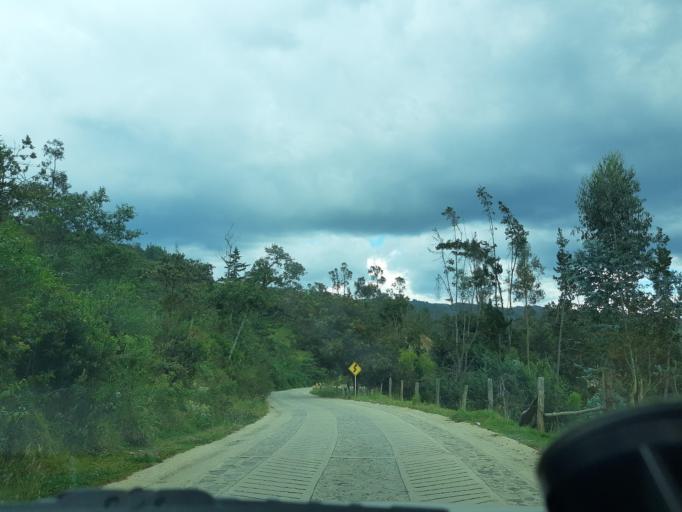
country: CO
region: Boyaca
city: Raquira
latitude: 5.5062
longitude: -73.7174
